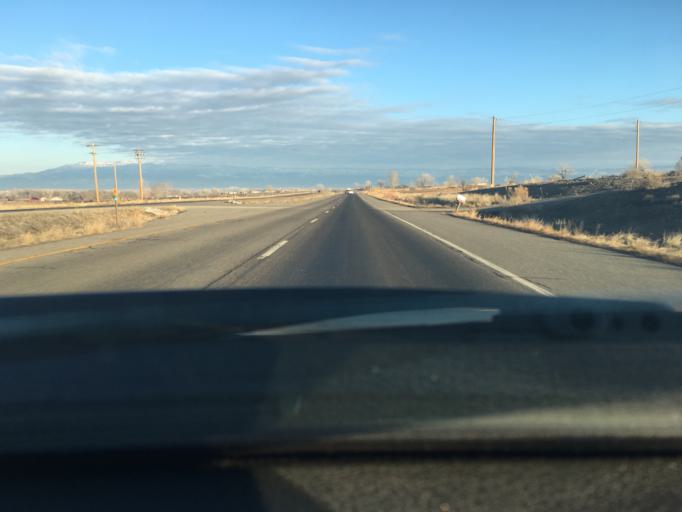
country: US
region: Colorado
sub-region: Montrose County
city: Olathe
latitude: 38.6235
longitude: -107.9849
